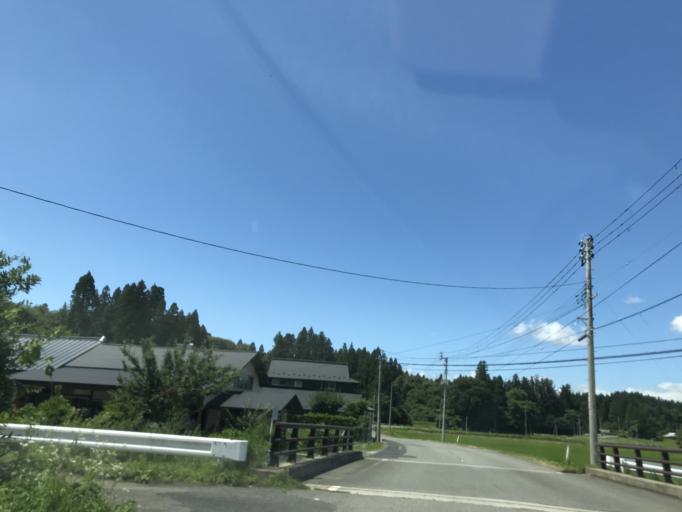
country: JP
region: Iwate
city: Ichinoseki
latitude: 38.9303
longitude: 141.0179
